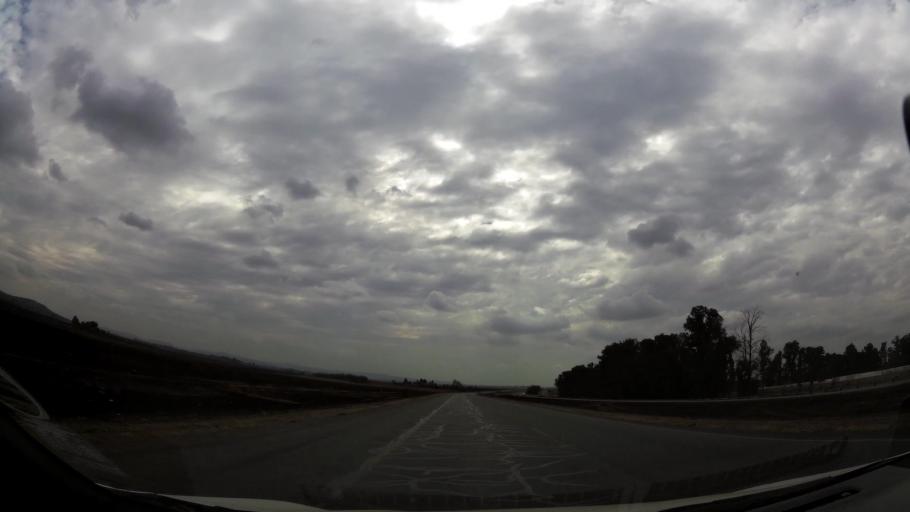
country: ZA
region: Gauteng
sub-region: Sedibeng District Municipality
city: Meyerton
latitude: -26.4067
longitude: 28.0788
